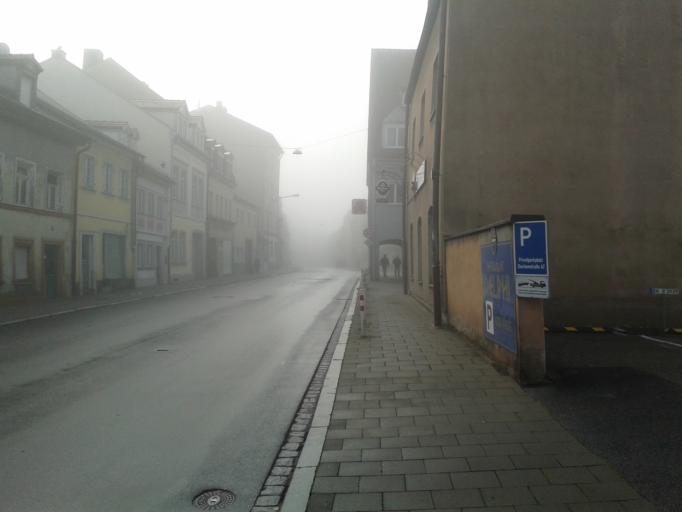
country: DE
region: Bavaria
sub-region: Upper Franconia
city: Bamberg
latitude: 49.9005
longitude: 10.8892
